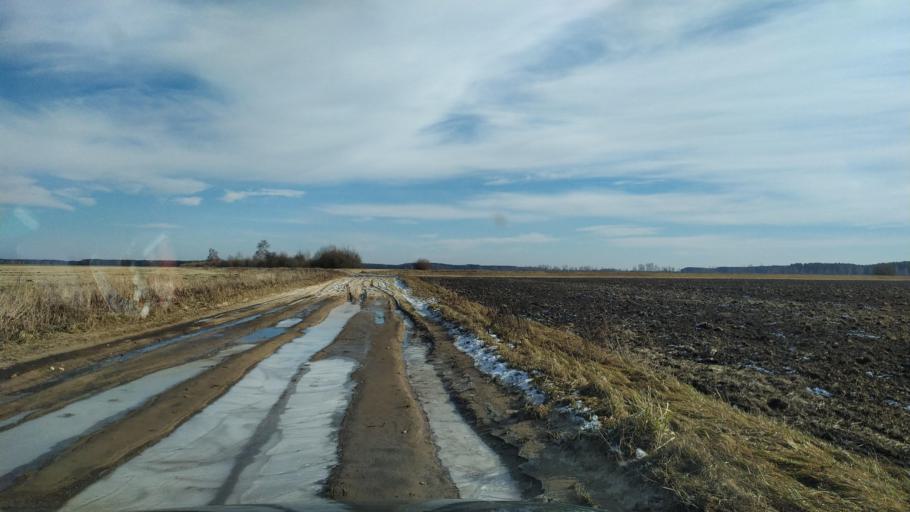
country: BY
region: Brest
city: Pruzhany
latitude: 52.5532
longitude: 24.3006
